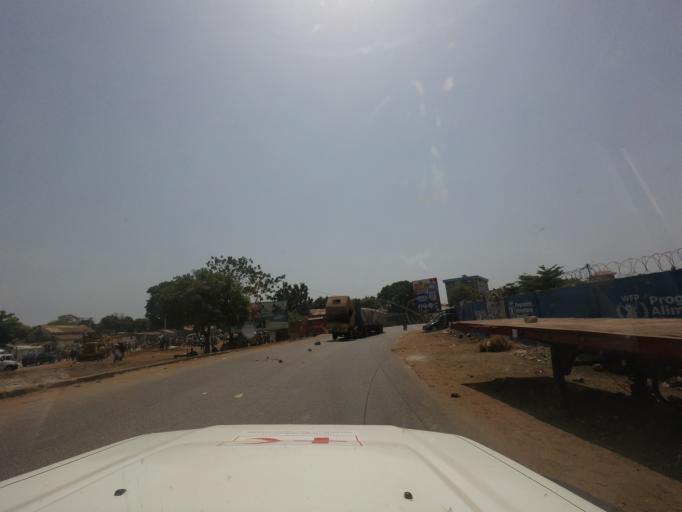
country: GN
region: Conakry
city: Camayenne
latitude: 9.5175
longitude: -13.6987
